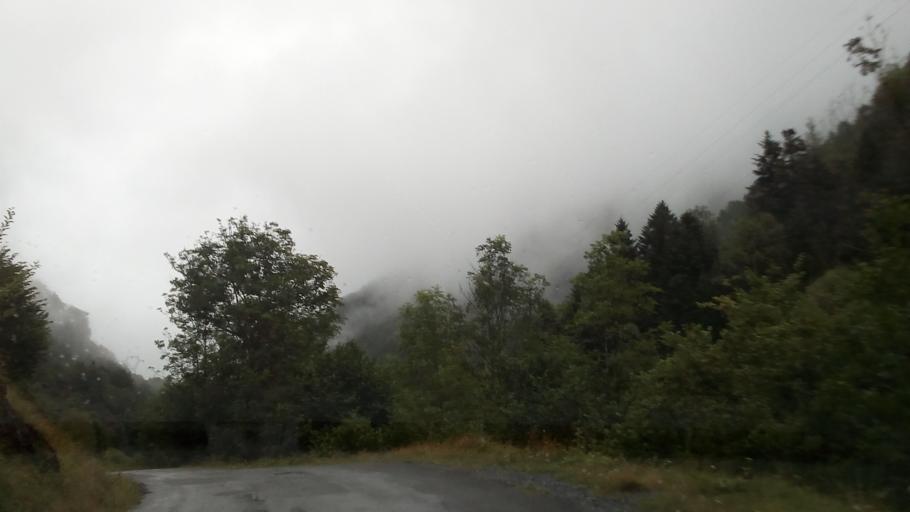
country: FR
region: Midi-Pyrenees
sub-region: Departement des Hautes-Pyrenees
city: Cauterets
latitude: 42.9306
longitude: -0.2441
